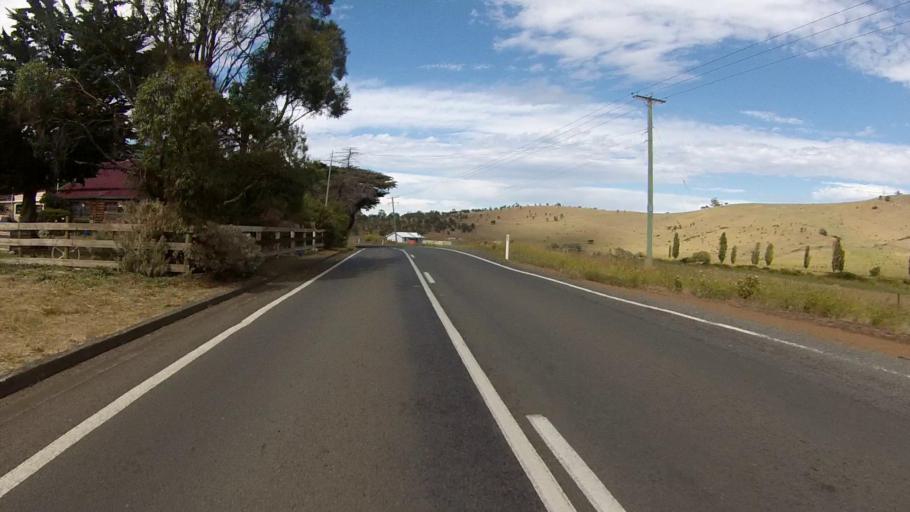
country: AU
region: Tasmania
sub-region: Brighton
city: Old Beach
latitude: -42.6762
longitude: 147.3568
